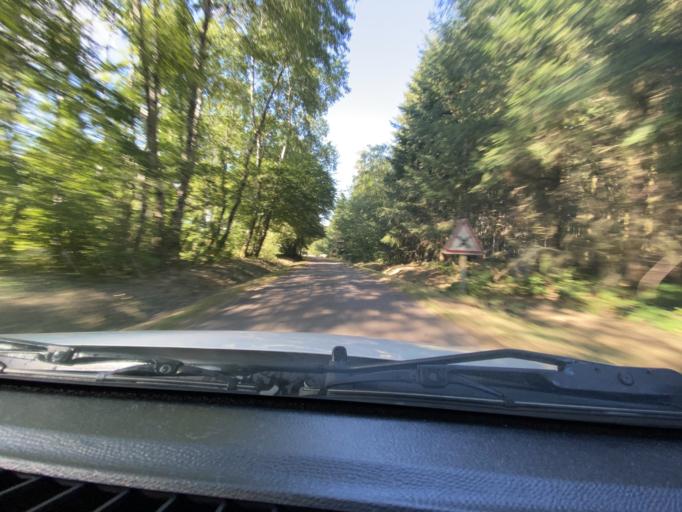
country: FR
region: Bourgogne
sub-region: Departement de la Cote-d'Or
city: Saulieu
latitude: 47.3072
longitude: 4.1827
